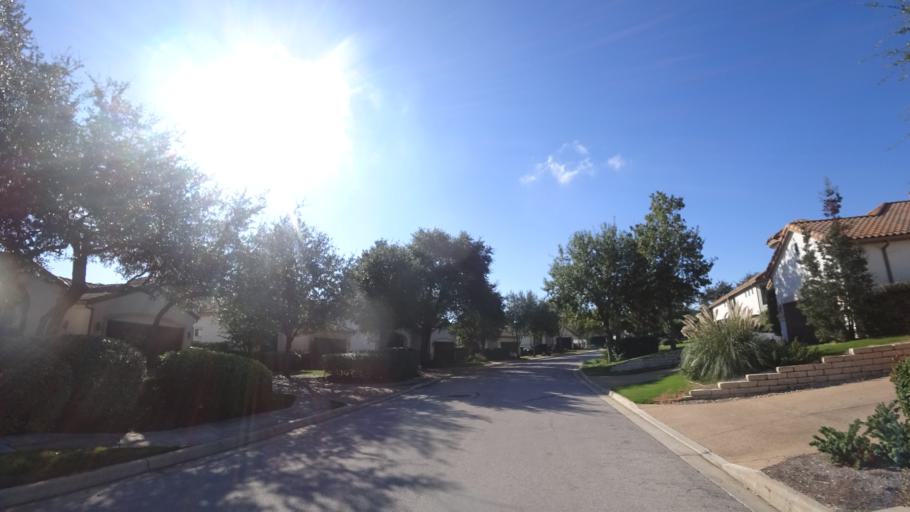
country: US
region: Texas
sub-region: Travis County
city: Bee Cave
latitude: 30.3512
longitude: -97.8913
